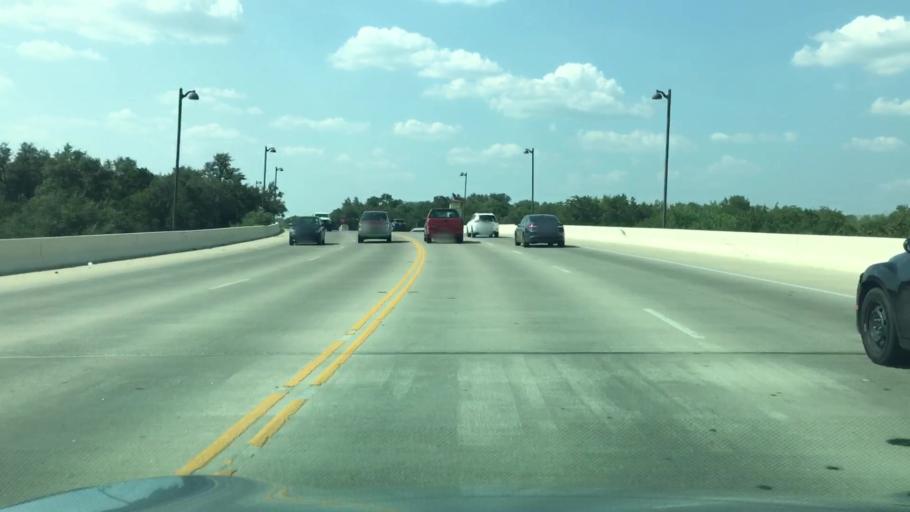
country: US
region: Texas
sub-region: Hays County
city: San Marcos
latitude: 29.8731
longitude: -97.9662
